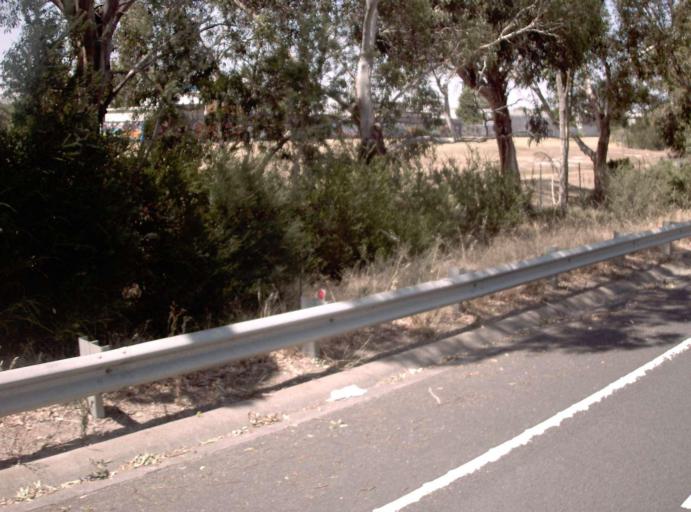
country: AU
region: Victoria
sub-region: Frankston
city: Seaford
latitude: -38.1128
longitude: 145.1380
